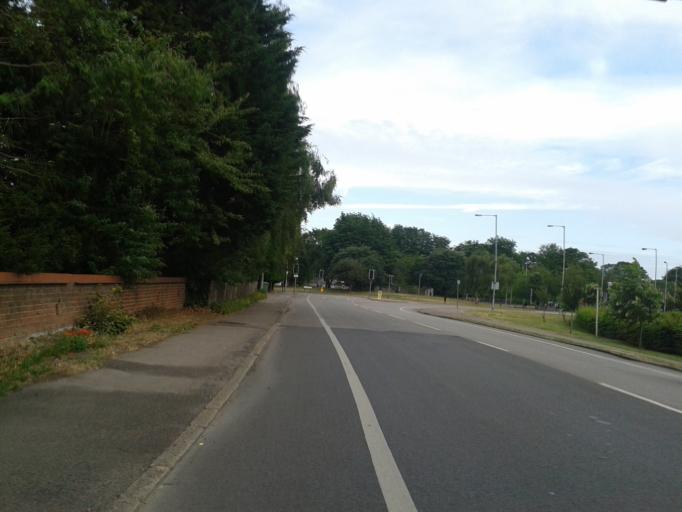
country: GB
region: England
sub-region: Cambridgeshire
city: Cambridge
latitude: 52.1774
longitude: 0.1441
